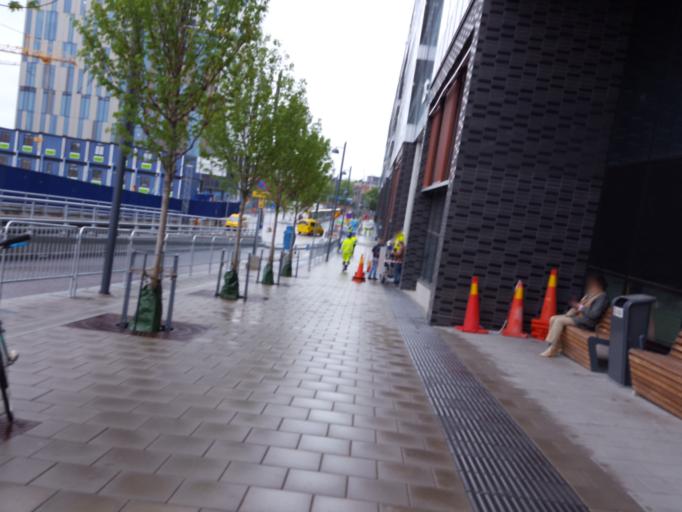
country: SE
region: Stockholm
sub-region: Norrtalje Kommun
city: Bergshamra
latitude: 59.3491
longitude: 18.0336
